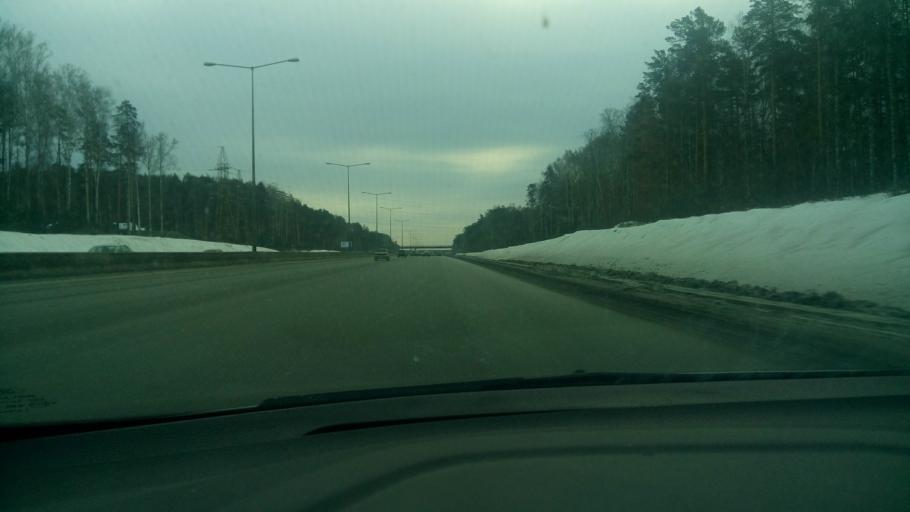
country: RU
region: Sverdlovsk
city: Istok
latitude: 56.7853
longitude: 60.6878
